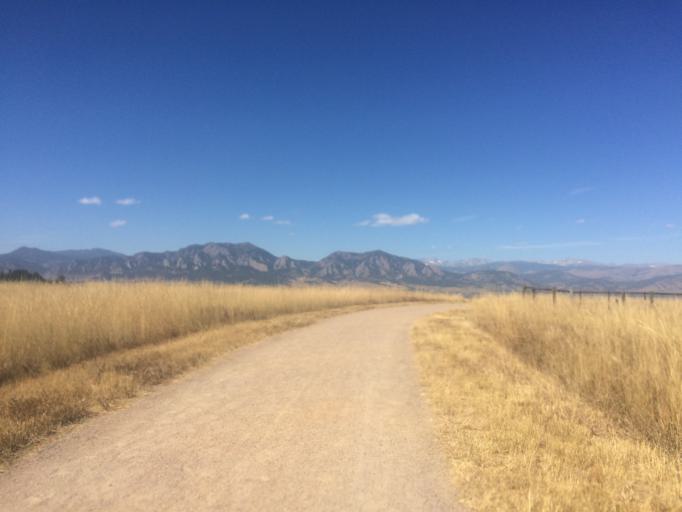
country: US
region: Colorado
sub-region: Boulder County
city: Superior
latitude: 39.9780
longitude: -105.1682
